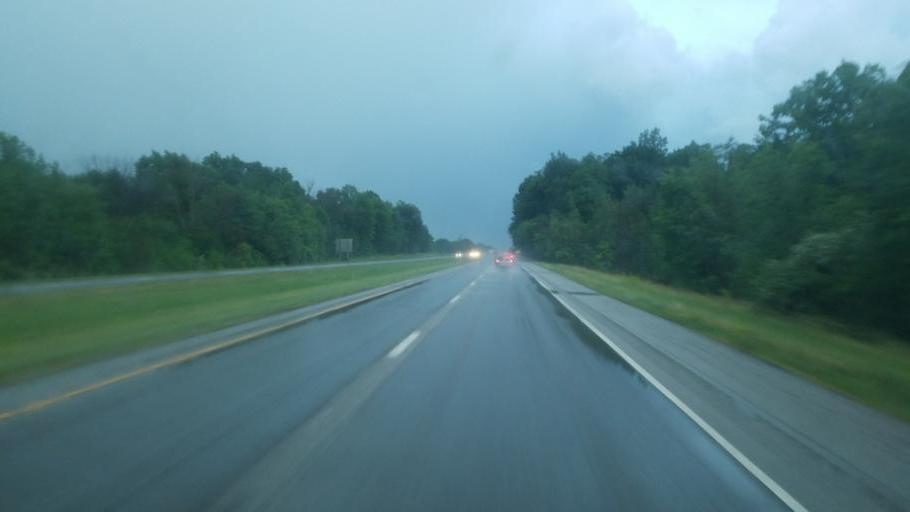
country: US
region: Ohio
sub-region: Wayne County
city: Doylestown
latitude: 40.9774
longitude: -81.6625
